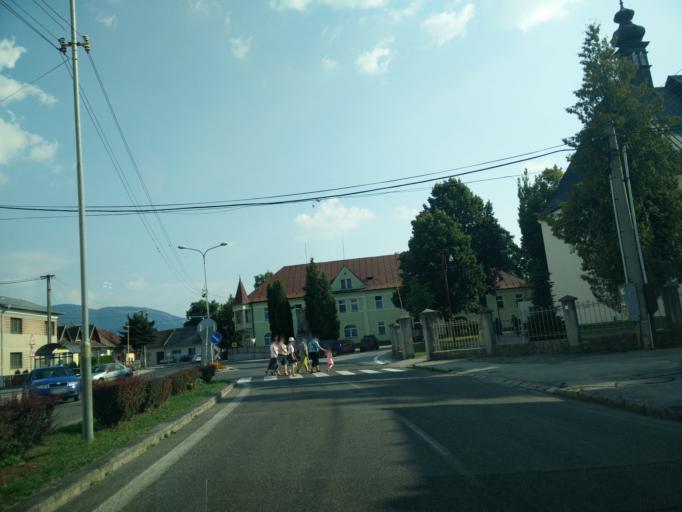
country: SK
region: Zilinsky
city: Rajec
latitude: 49.0877
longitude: 18.6334
